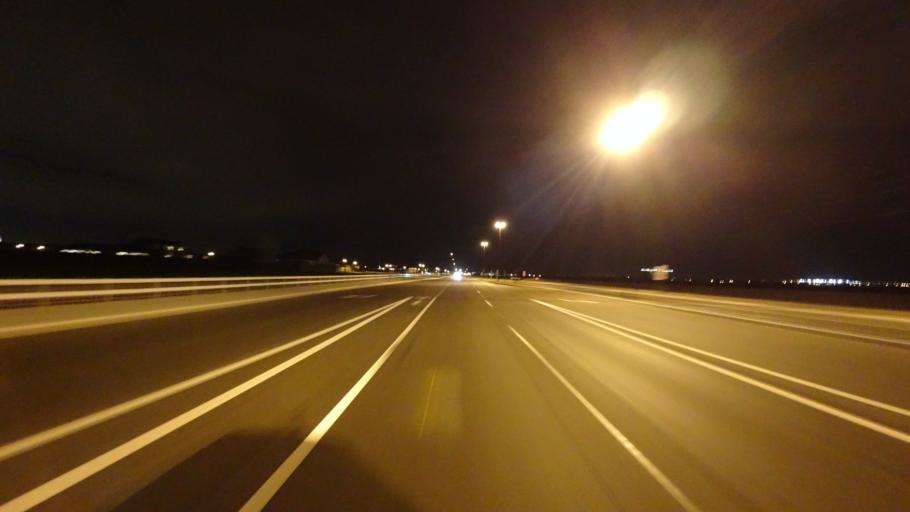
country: US
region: Arizona
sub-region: Maricopa County
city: Gilbert
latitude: 33.3367
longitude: -111.7213
